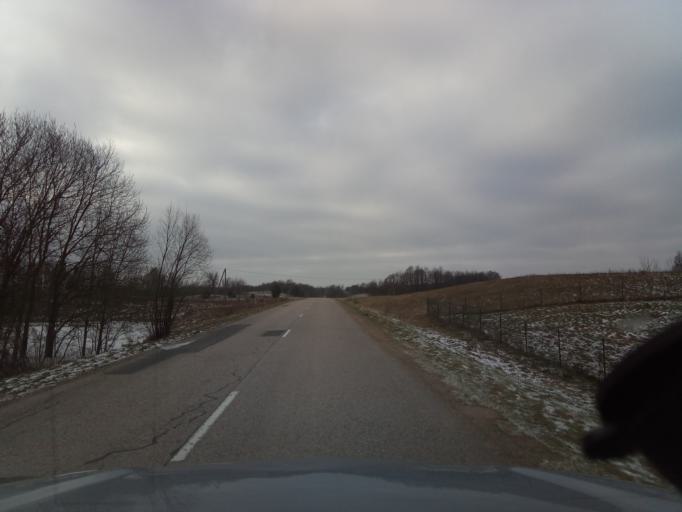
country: LT
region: Alytaus apskritis
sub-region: Alytaus rajonas
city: Daugai
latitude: 54.3490
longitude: 24.3202
